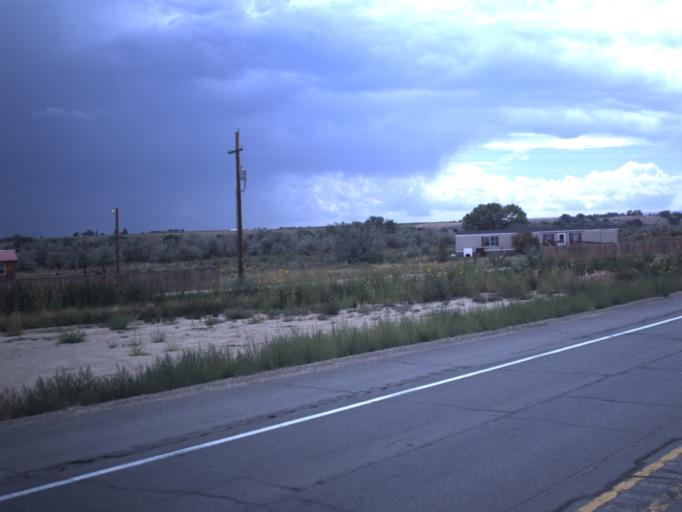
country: US
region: Utah
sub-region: Duchesne County
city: Roosevelt
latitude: 40.1936
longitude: -110.0744
